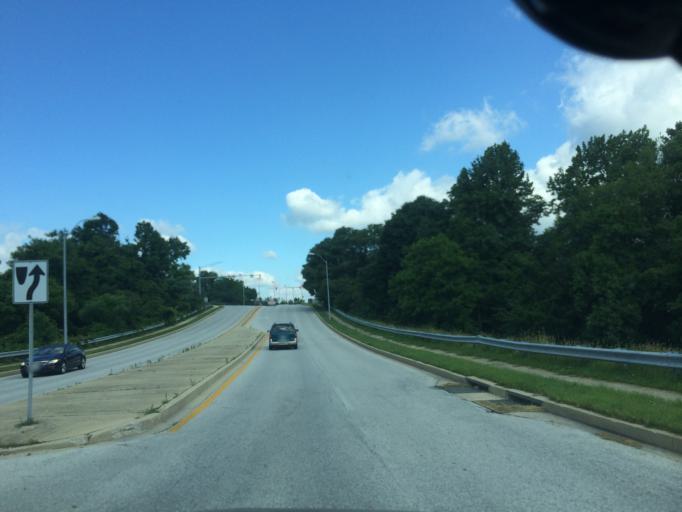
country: US
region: Maryland
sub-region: Carroll County
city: Westminster
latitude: 39.5670
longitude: -76.9707
